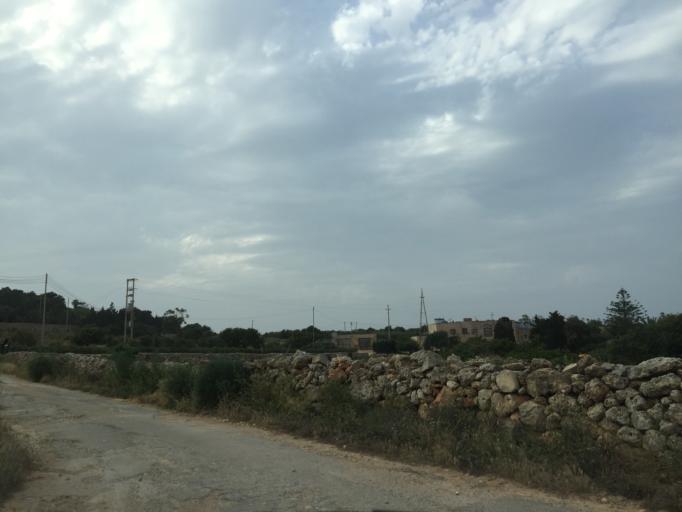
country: MT
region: L-Imgarr
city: Imgarr
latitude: 35.9326
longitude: 14.3869
